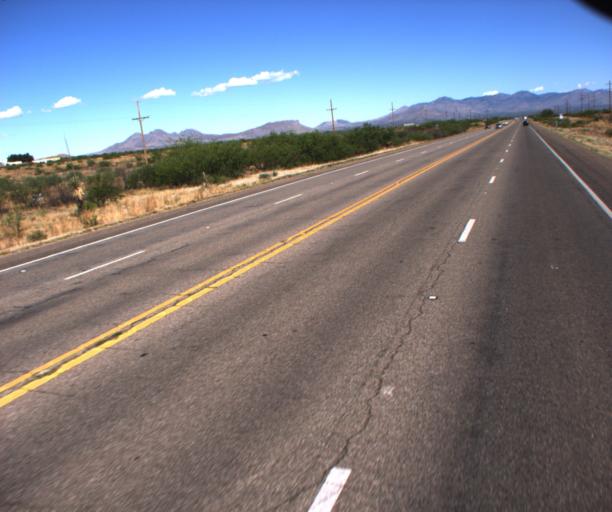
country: US
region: Arizona
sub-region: Cochise County
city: Sierra Vista
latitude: 31.5889
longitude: -110.3220
